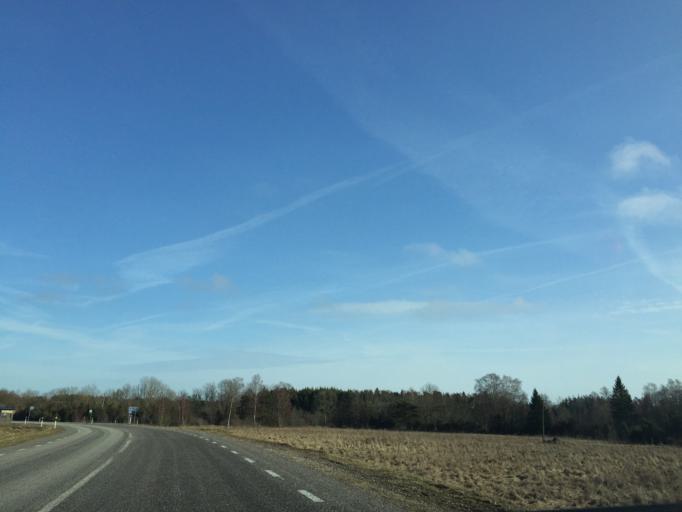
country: EE
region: Saare
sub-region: Kuressaare linn
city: Kuressaare
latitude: 58.4640
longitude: 22.0034
